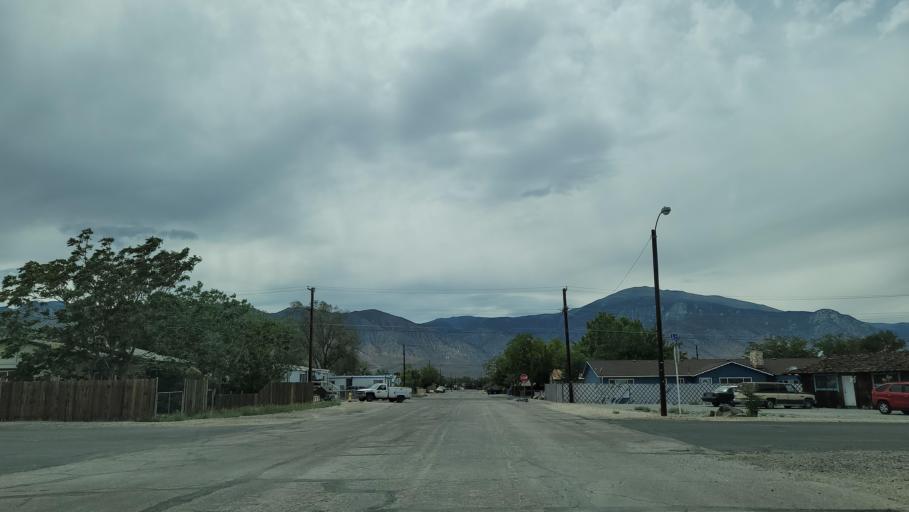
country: US
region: Nevada
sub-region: Mineral County
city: Hawthorne
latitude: 38.5292
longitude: -118.6178
